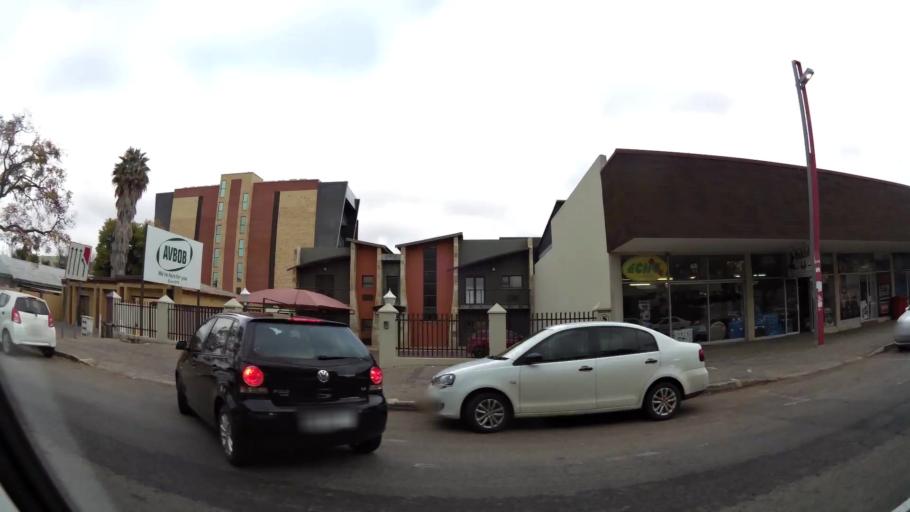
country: ZA
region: Limpopo
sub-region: Capricorn District Municipality
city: Polokwane
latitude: -23.9166
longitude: 29.4544
